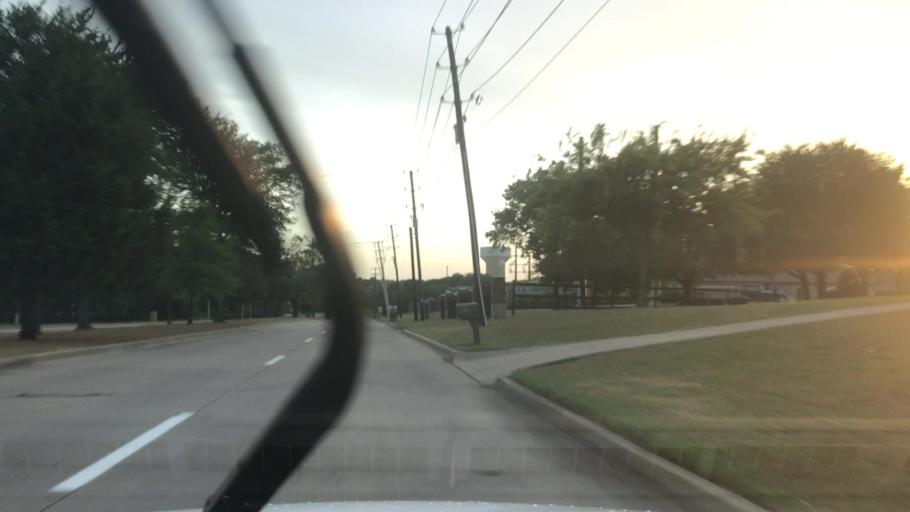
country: US
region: Texas
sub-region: Dallas County
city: Balch Springs
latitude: 32.7077
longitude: -96.5608
